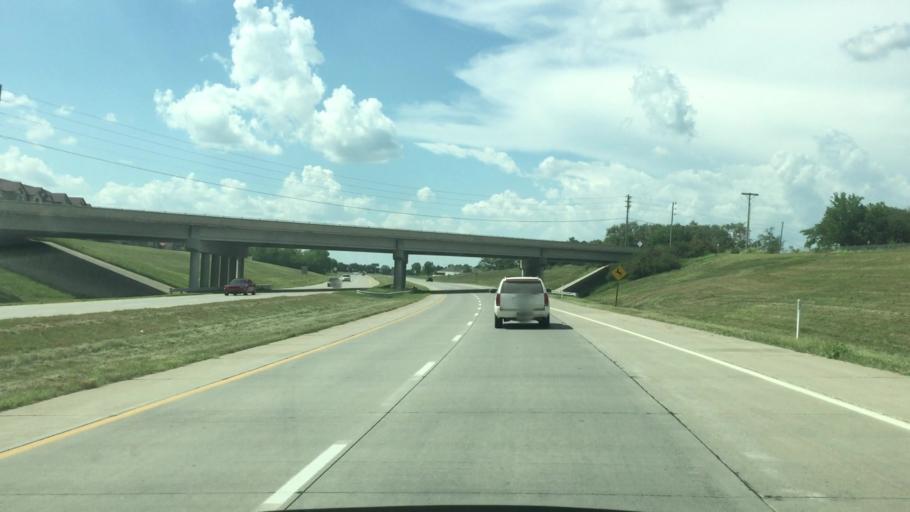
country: US
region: Kansas
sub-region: Butler County
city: Andover
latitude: 37.6949
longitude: -97.1885
